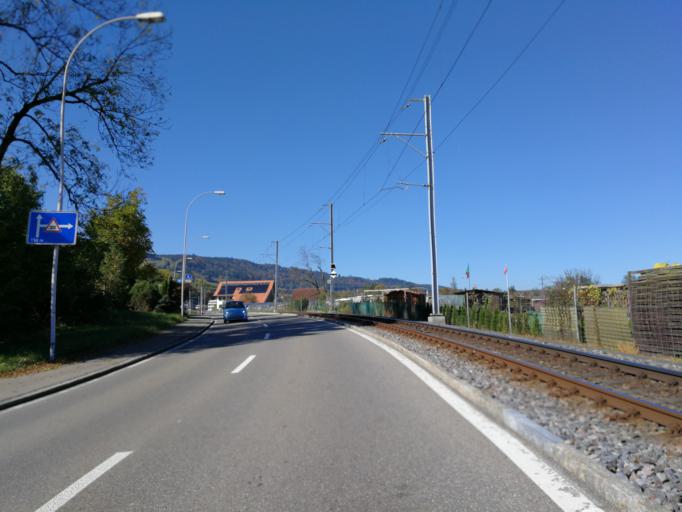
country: CH
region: Zurich
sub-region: Bezirk Uster
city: Esslingen
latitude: 47.2920
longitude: 8.7049
